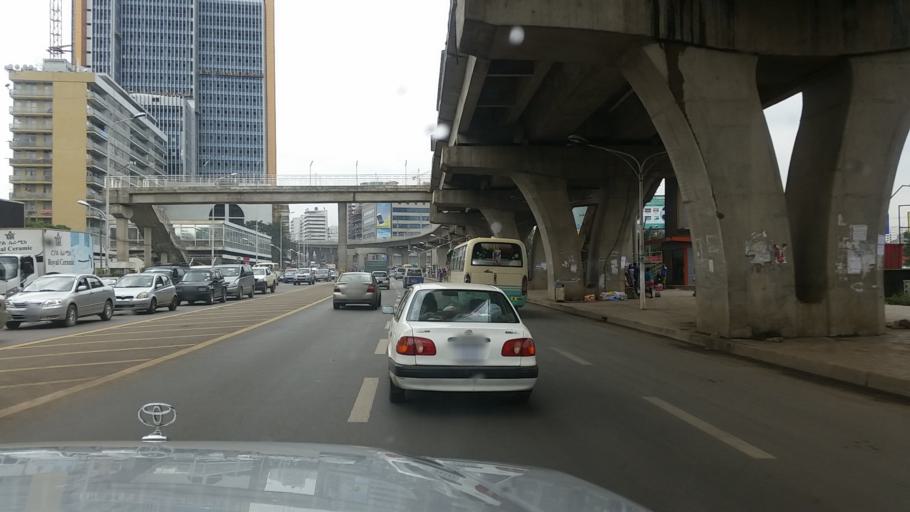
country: ET
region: Adis Abeba
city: Addis Ababa
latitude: 9.0118
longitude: 38.7582
